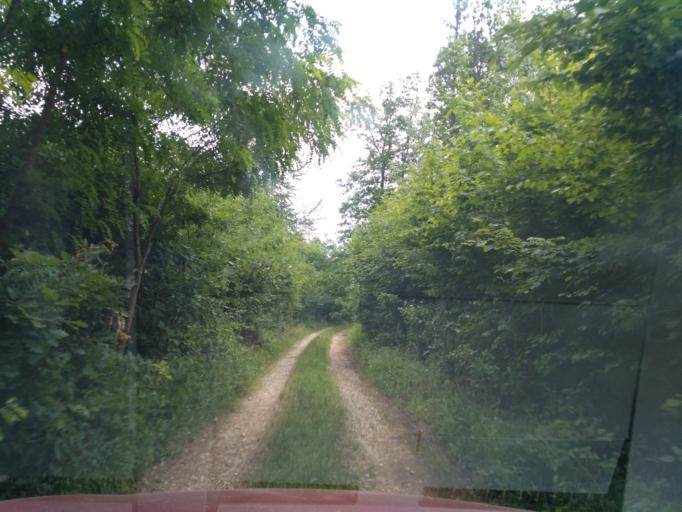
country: SK
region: Kosicky
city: Moldava nad Bodvou
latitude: 48.6552
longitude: 21.0460
